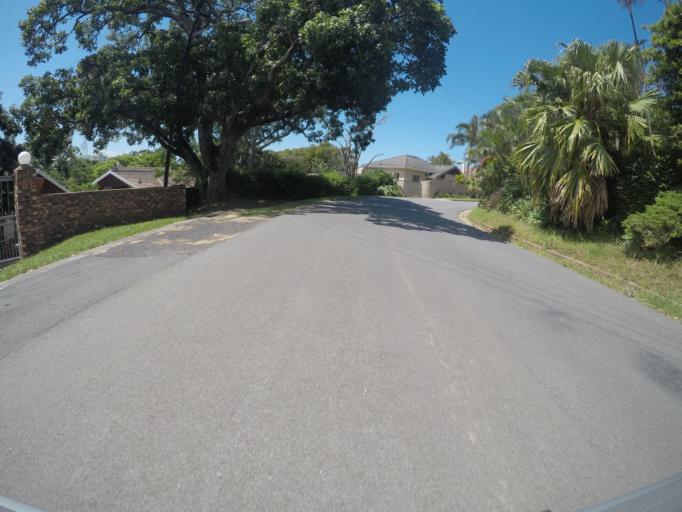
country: ZA
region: Eastern Cape
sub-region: Buffalo City Metropolitan Municipality
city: East London
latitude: -32.9747
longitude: 27.9035
